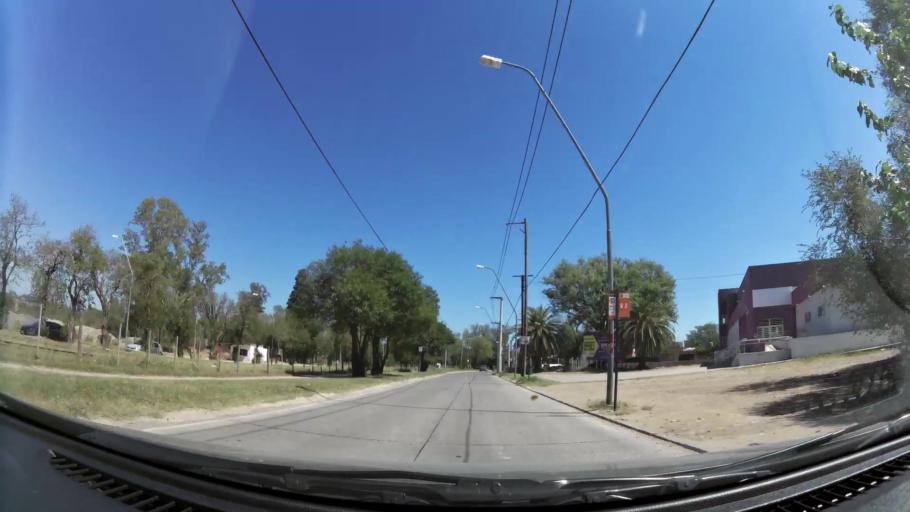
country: AR
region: Cordoba
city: Villa Allende
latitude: -31.3354
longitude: -64.2748
